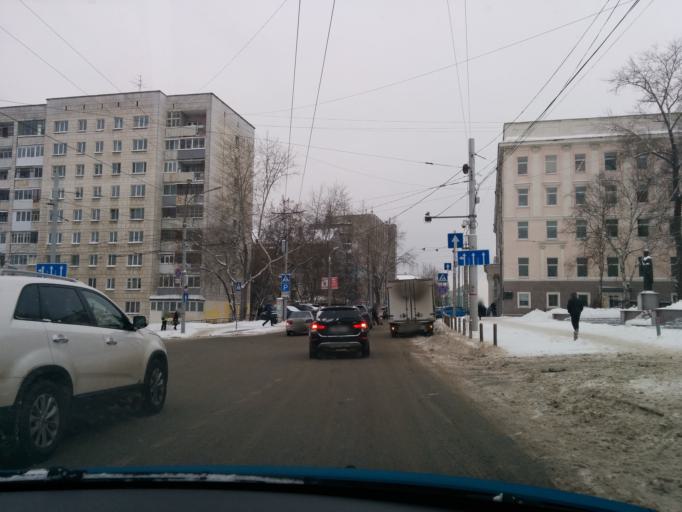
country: RU
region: Perm
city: Perm
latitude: 58.0158
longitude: 56.2351
